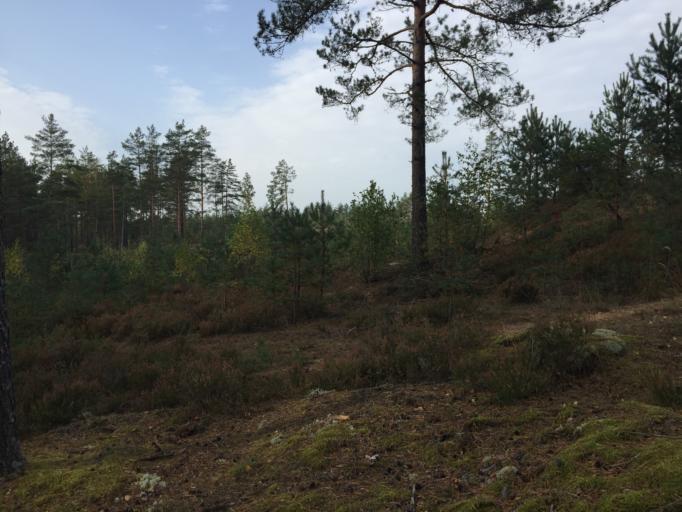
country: LV
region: Garkalne
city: Garkalne
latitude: 56.9560
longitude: 24.4177
